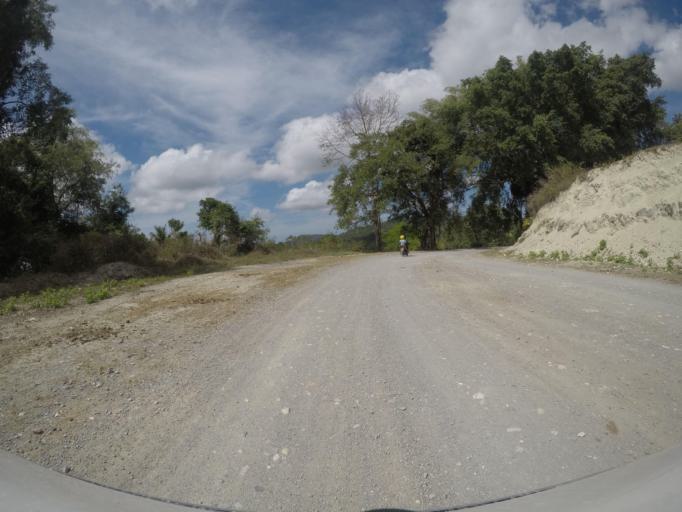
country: TL
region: Viqueque
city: Viqueque
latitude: -8.8709
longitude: 126.3450
